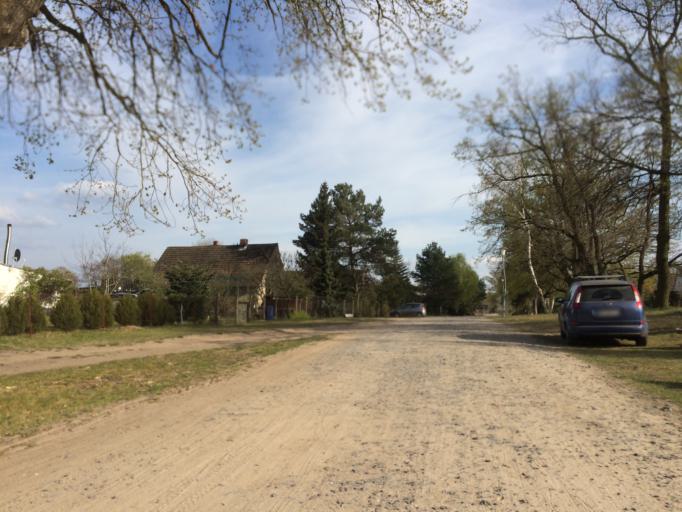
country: DE
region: Berlin
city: Buch
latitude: 52.6791
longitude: 13.4771
